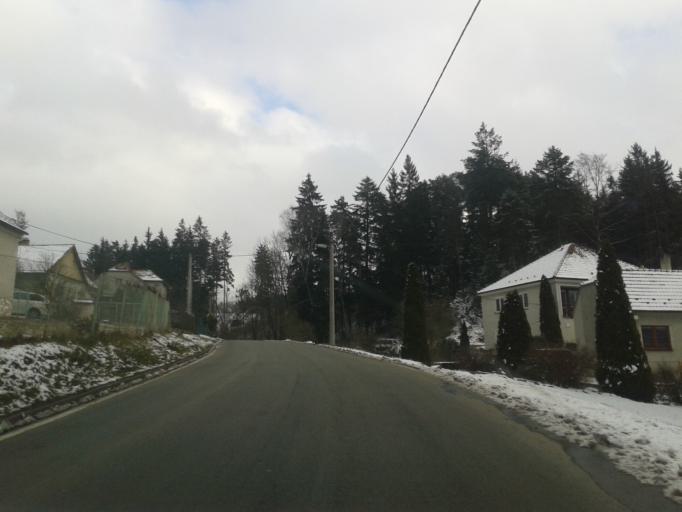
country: CZ
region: Olomoucky
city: Horni Stepanov
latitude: 49.5596
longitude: 16.8029
